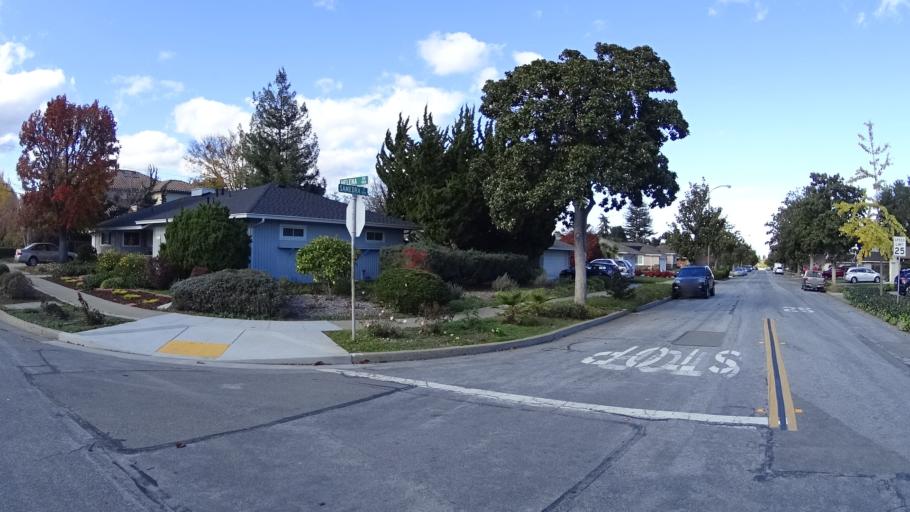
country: US
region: California
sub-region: Santa Clara County
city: Cupertino
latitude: 37.3411
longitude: -122.0511
